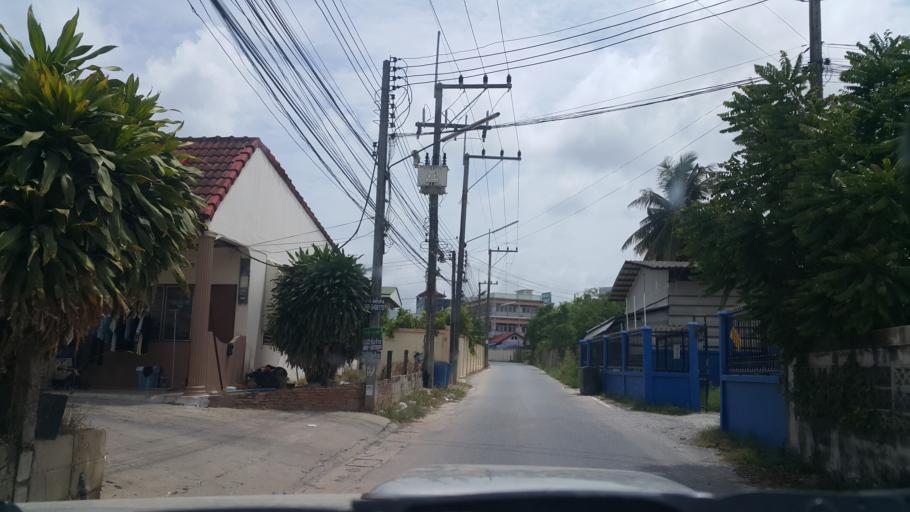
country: TH
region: Rayong
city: Ban Chang
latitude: 12.7250
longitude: 101.0590
